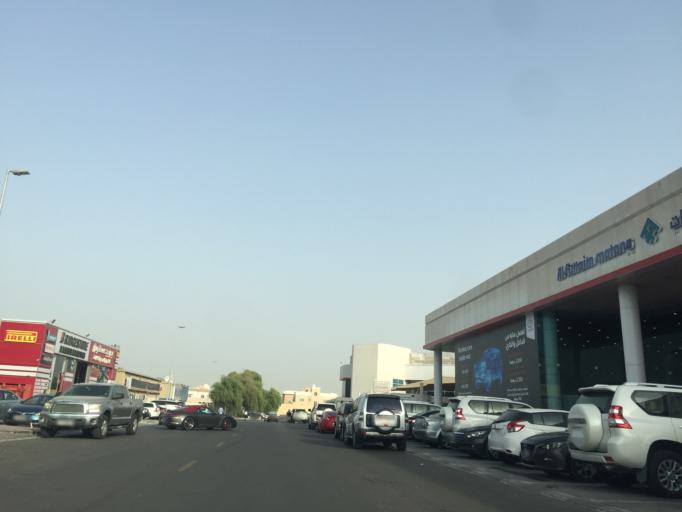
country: AE
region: Dubai
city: Dubai
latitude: 25.1762
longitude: 55.2471
